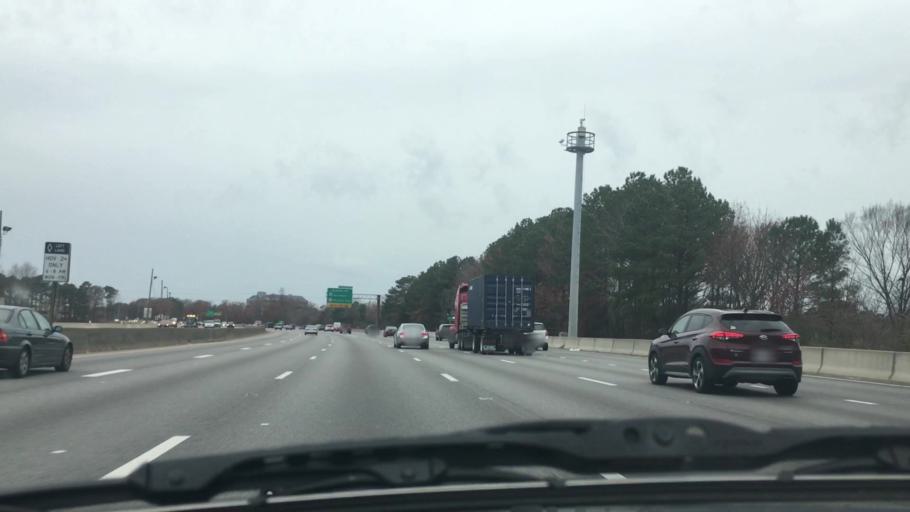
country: US
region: Virginia
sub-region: City of Chesapeake
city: Chesapeake
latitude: 36.8443
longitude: -76.1690
